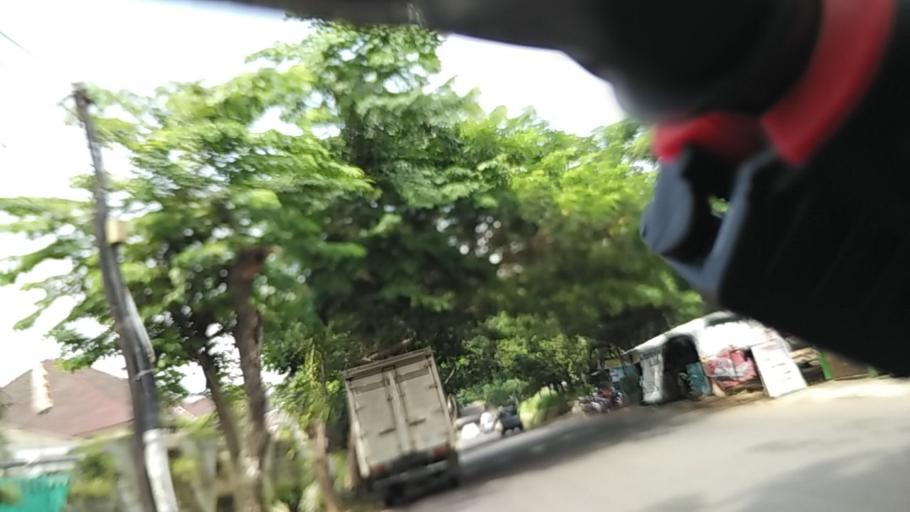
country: ID
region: Central Java
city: Semarang
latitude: -7.0092
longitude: 110.4236
